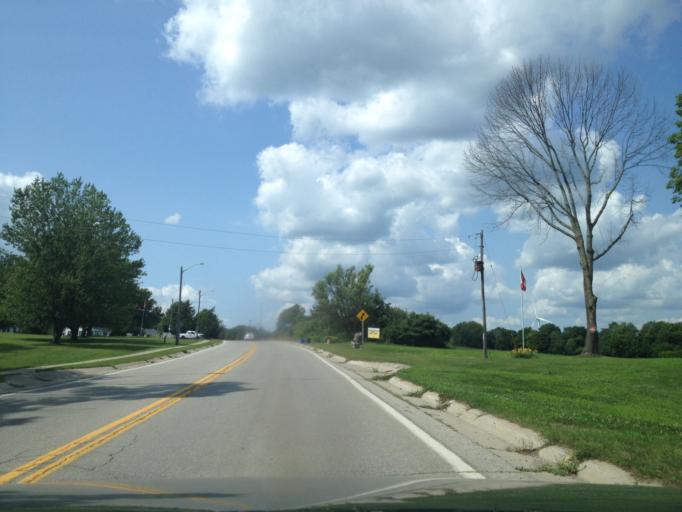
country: CA
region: Ontario
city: Aylmer
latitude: 42.6507
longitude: -80.8087
